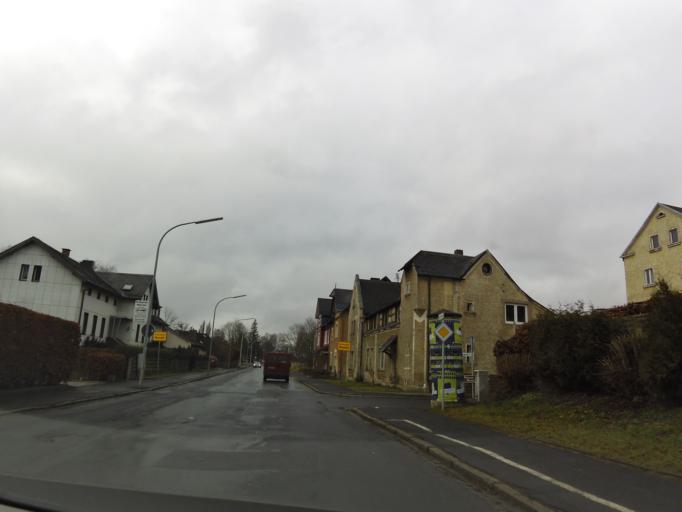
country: DE
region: Bavaria
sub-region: Upper Franconia
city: Wunsiedel
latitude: 50.0441
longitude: 12.0249
